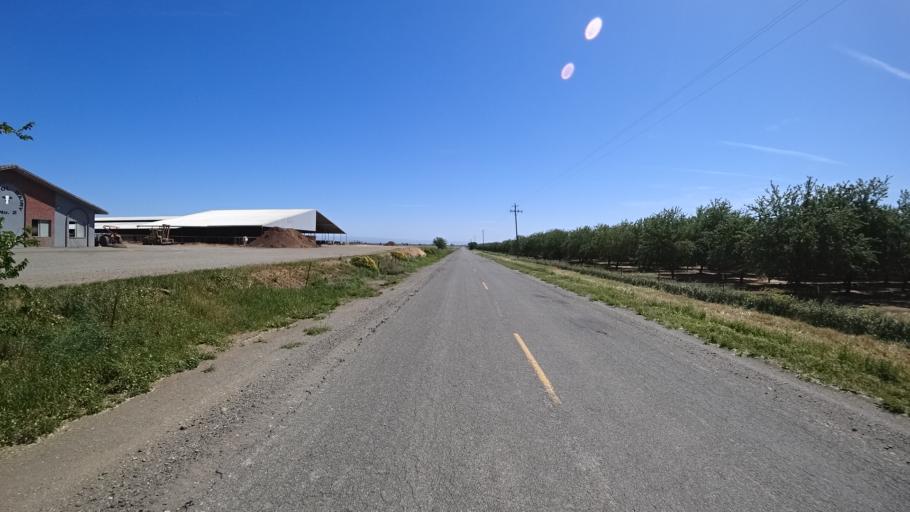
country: US
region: California
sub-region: Glenn County
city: Orland
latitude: 39.6530
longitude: -122.1663
